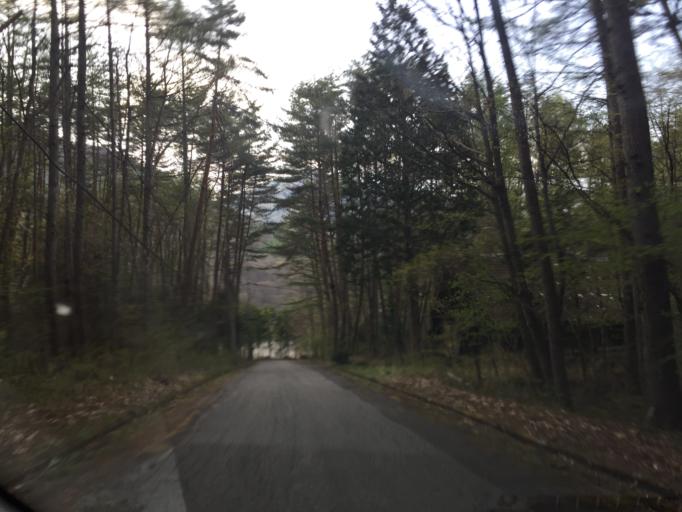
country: JP
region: Gifu
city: Nakatsugawa
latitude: 35.3557
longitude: 137.6733
